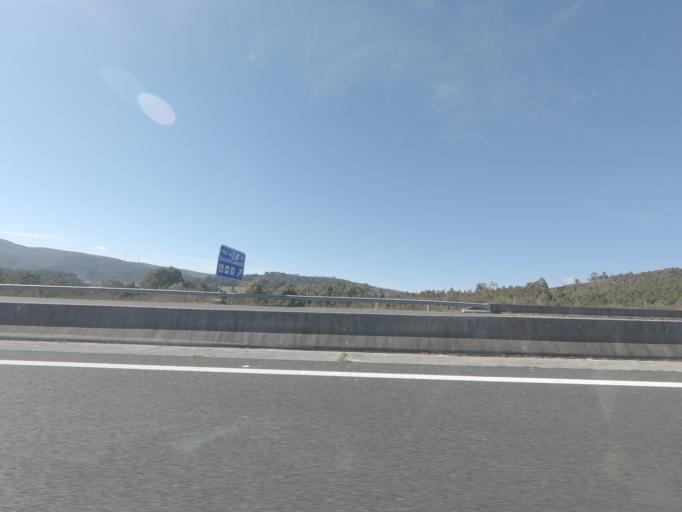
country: ES
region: Galicia
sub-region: Provincia de Ourense
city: Pinor
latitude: 42.5302
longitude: -8.0157
